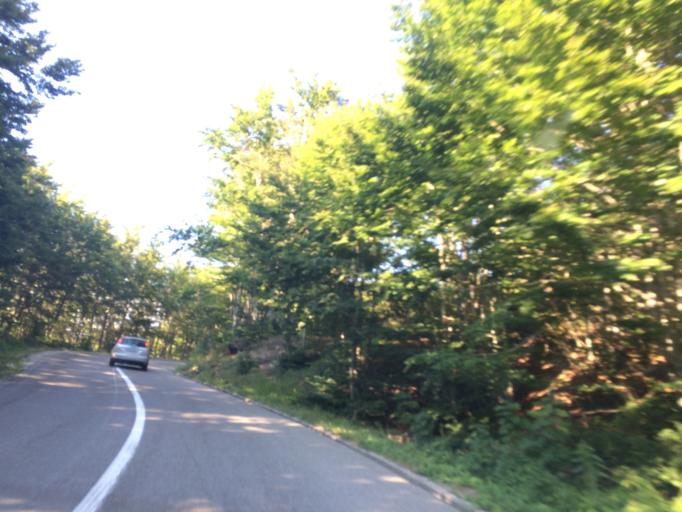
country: ME
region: Opstina Savnik
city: Savnik
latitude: 42.9059
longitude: 19.0914
